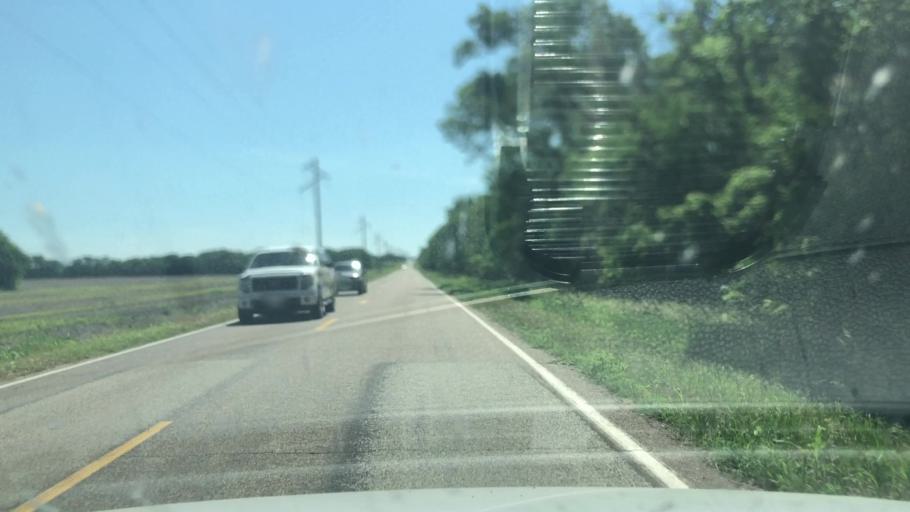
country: US
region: Kansas
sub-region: Cowley County
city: Winfield
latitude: 37.3609
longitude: -97.0034
